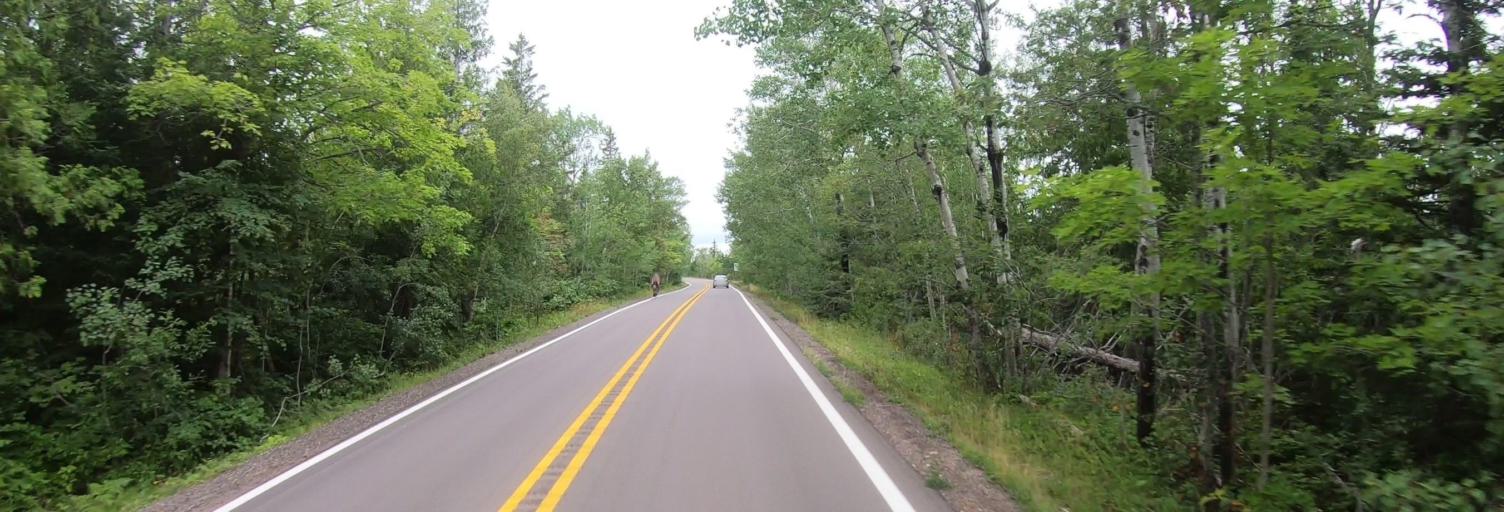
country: US
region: Michigan
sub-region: Keweenaw County
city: Eagle River
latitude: 47.4771
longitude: -88.0025
